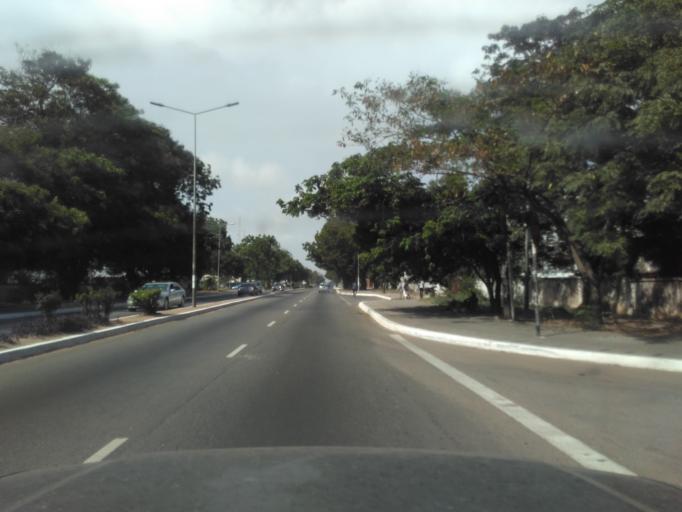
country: GH
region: Greater Accra
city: Accra
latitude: 5.5616
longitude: -0.1959
